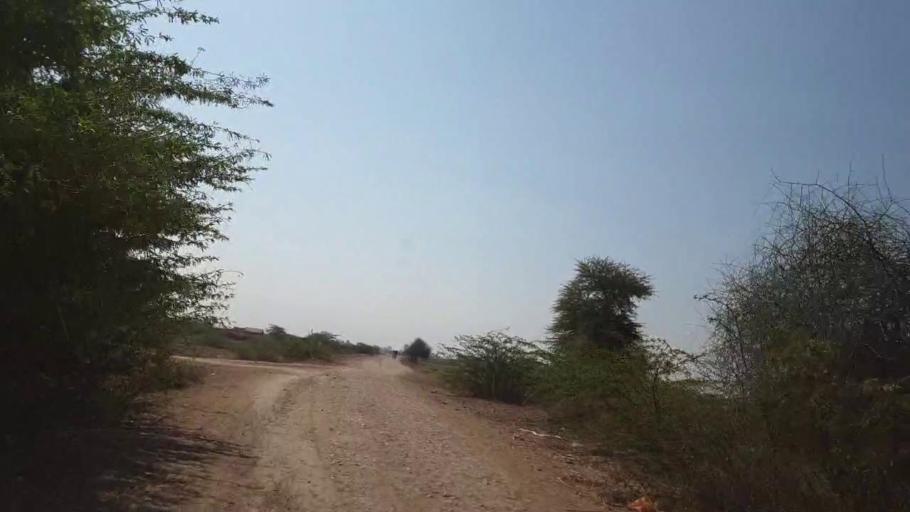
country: PK
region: Sindh
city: Kunri
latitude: 25.1606
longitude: 69.5277
